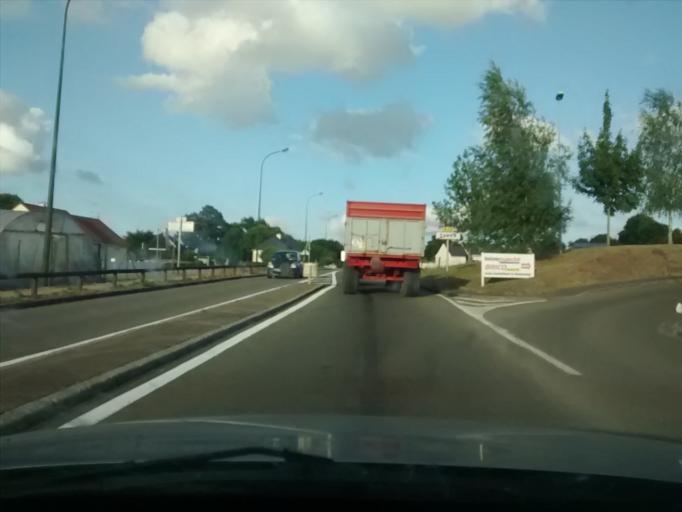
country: FR
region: Pays de la Loire
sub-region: Departement de la Mayenne
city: Evron
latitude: 48.1561
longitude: -0.3825
